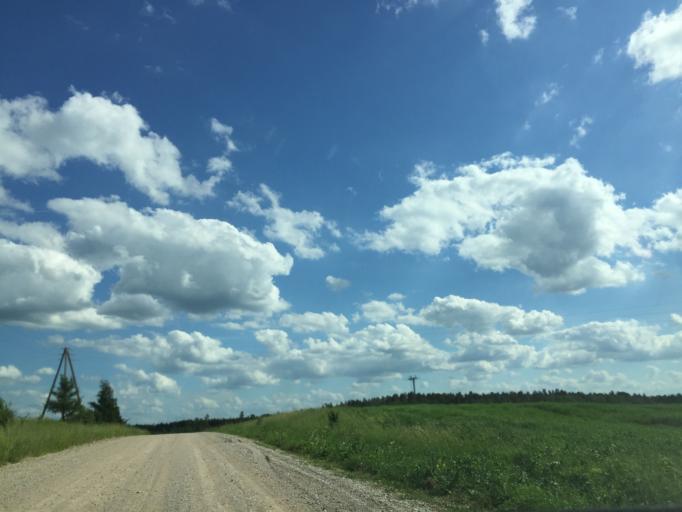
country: LV
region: Jaunpils
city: Jaunpils
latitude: 56.8153
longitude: 23.0713
